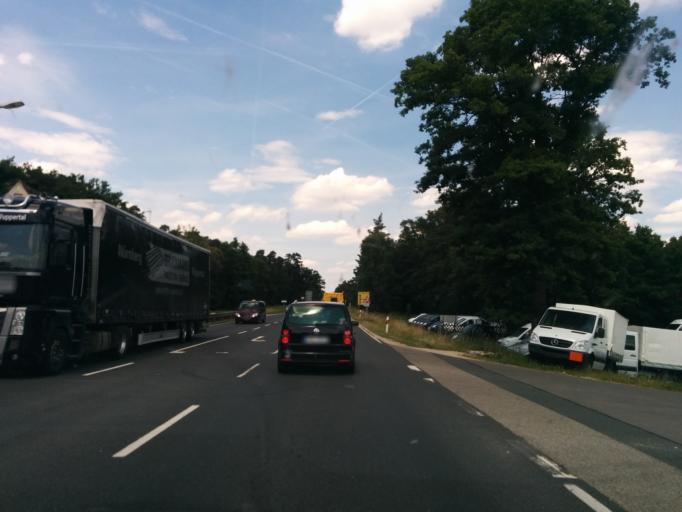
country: DE
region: Bavaria
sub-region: Regierungsbezirk Mittelfranken
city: Roth
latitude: 49.2107
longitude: 11.0794
